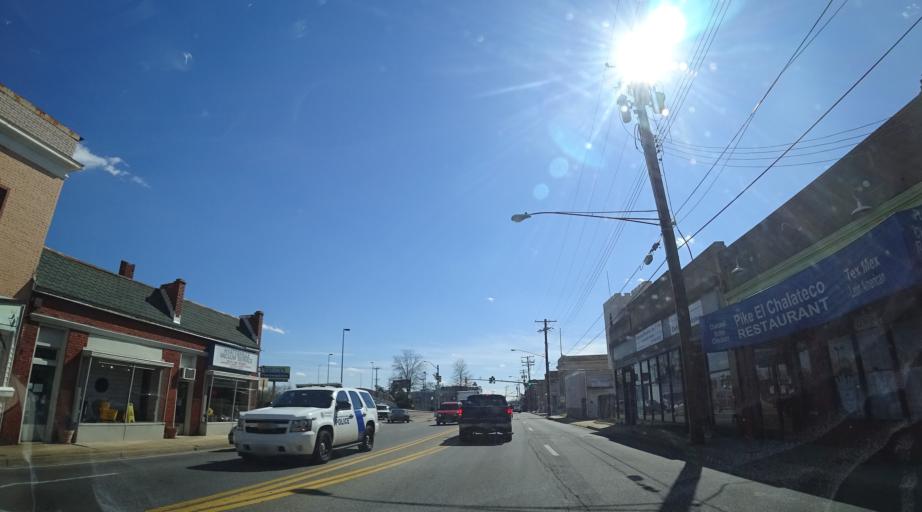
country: US
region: Maryland
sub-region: Prince George's County
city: Hyattsville
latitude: 38.9541
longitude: -76.9404
